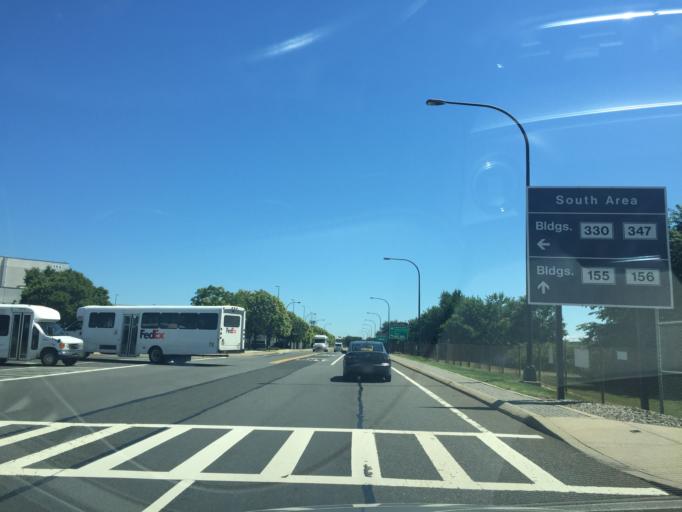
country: US
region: New Jersey
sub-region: Union County
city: Elizabeth
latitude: 40.6772
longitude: -74.1871
